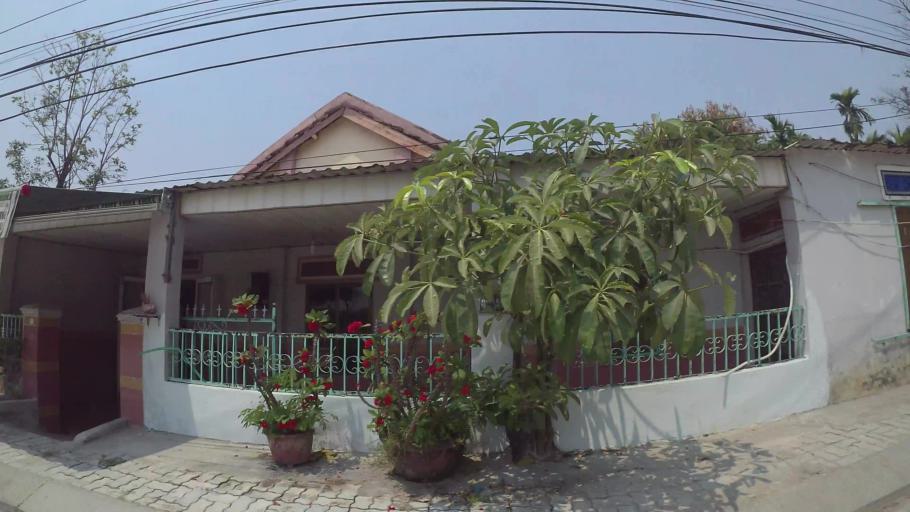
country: VN
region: Da Nang
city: Cam Le
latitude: 16.0195
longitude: 108.2137
